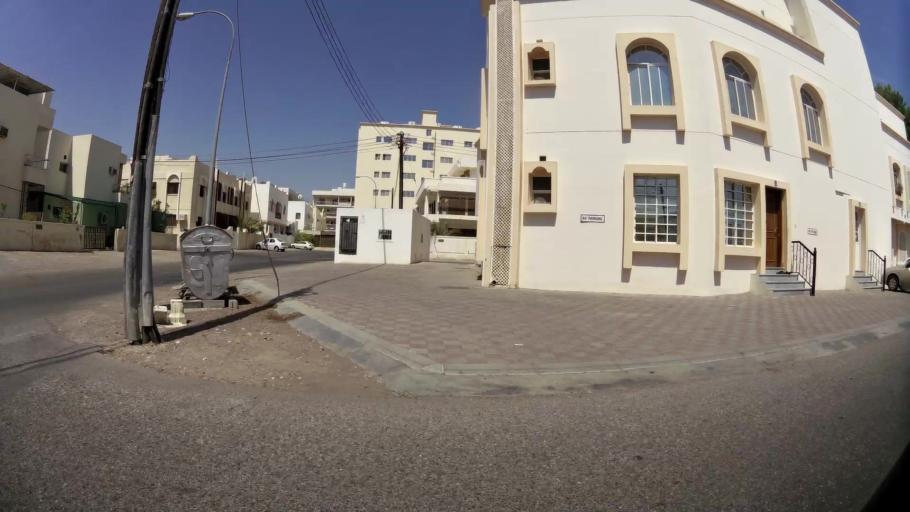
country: OM
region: Muhafazat Masqat
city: Muscat
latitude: 23.5999
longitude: 58.5430
